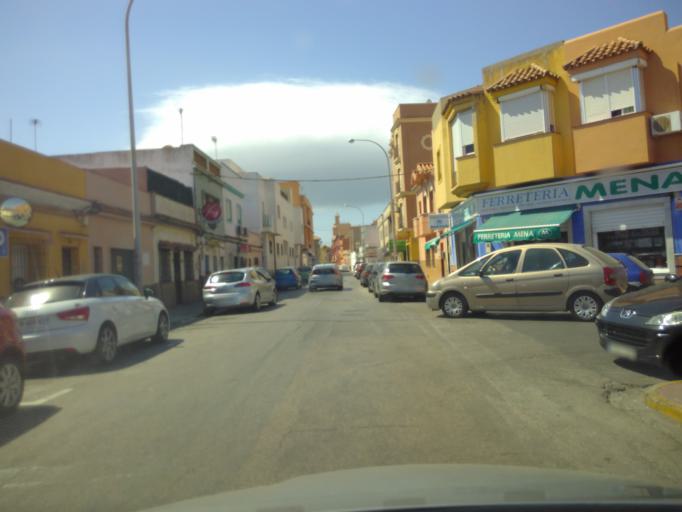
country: ES
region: Andalusia
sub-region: Provincia de Cadiz
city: La Linea de la Concepcion
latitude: 36.1686
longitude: -5.3492
